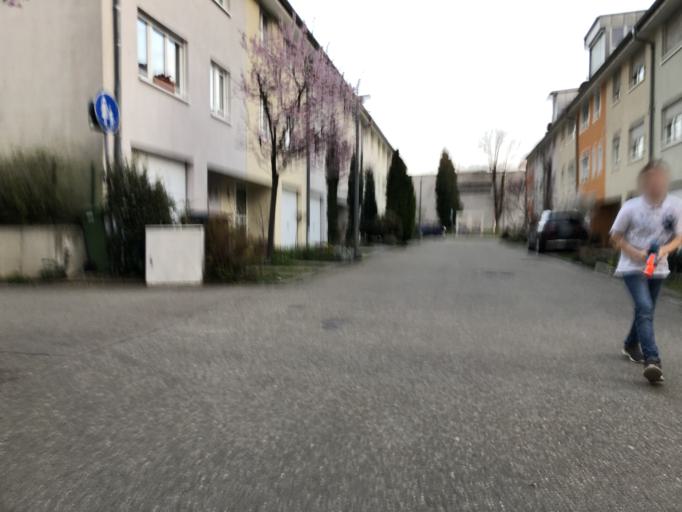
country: DE
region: Baden-Wuerttemberg
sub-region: Freiburg Region
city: Merzhausen
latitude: 47.9860
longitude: 7.8213
